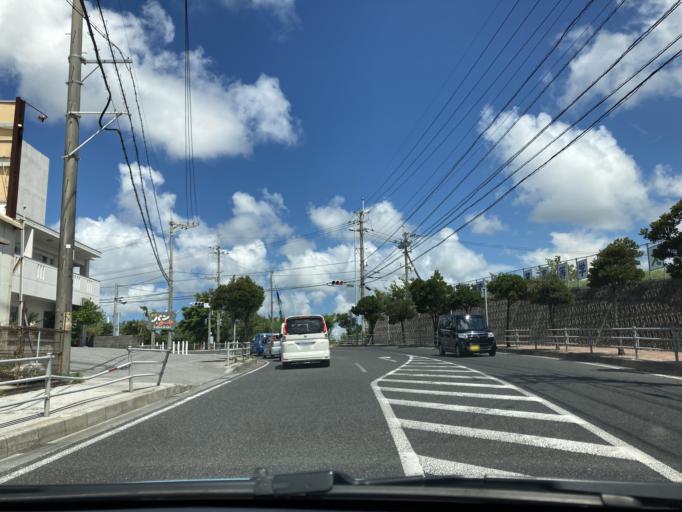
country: JP
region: Okinawa
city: Tomigusuku
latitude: 26.1713
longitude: 127.7221
